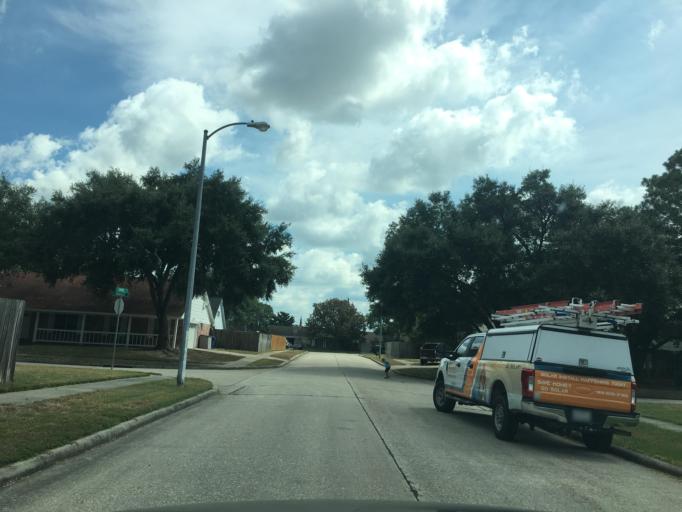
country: US
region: Texas
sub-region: Harris County
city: Spring
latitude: 30.1161
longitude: -95.3980
